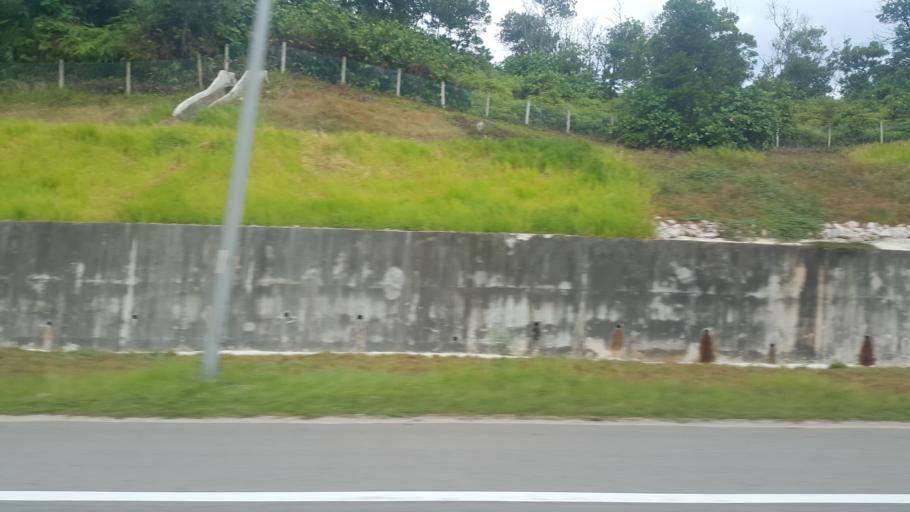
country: MY
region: Johor
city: Pekan Nenas
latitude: 1.4229
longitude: 103.6010
